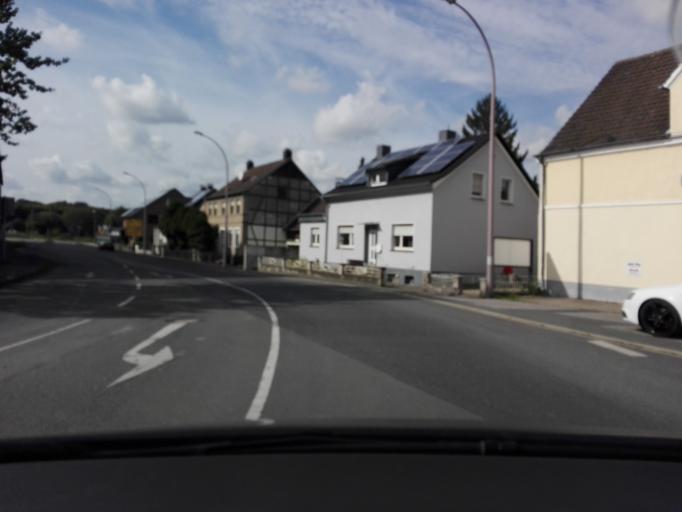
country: DE
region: North Rhine-Westphalia
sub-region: Regierungsbezirk Arnsberg
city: Holzwickede
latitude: 51.5479
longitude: 7.6395
